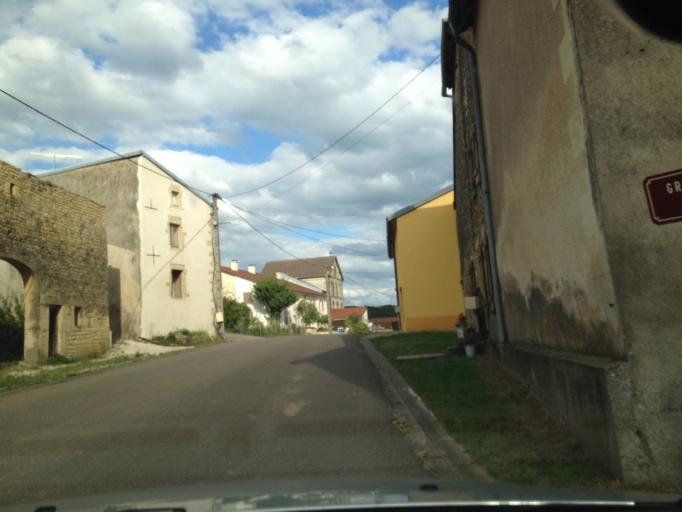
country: FR
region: Franche-Comte
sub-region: Departement de la Haute-Saone
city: Jussey
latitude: 47.8568
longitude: 5.9783
